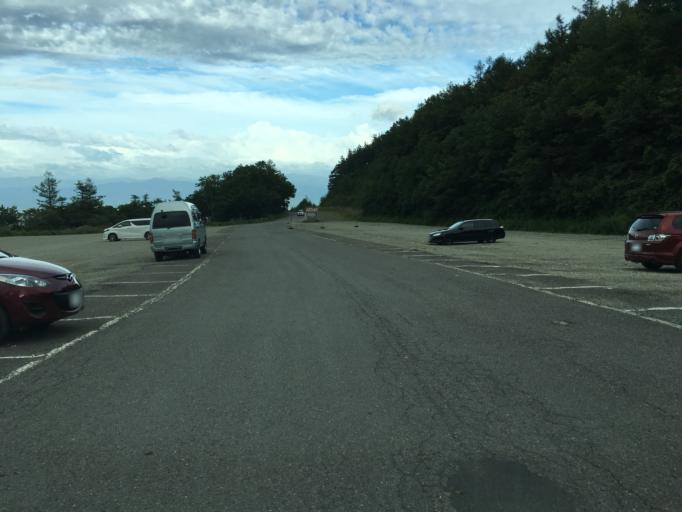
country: JP
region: Fukushima
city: Nihommatsu
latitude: 37.6228
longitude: 140.3259
